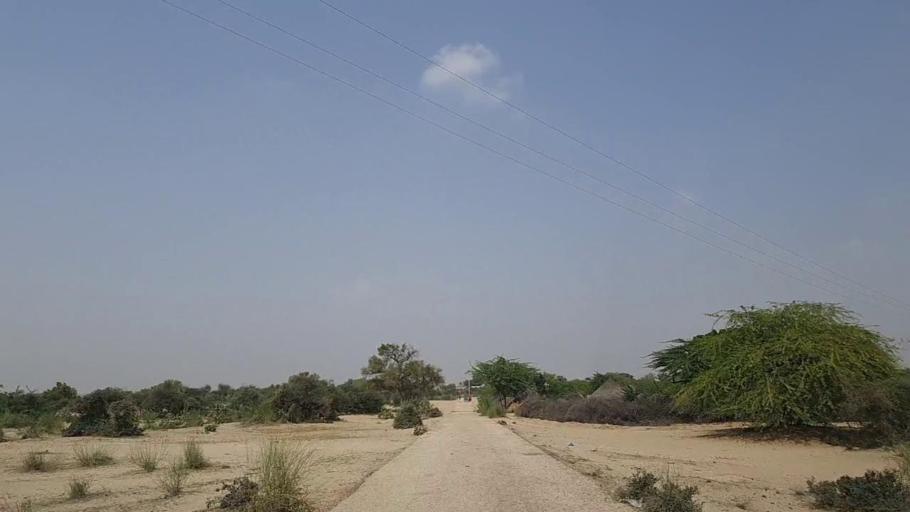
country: PK
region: Sindh
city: Mithi
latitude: 24.7602
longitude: 69.9266
